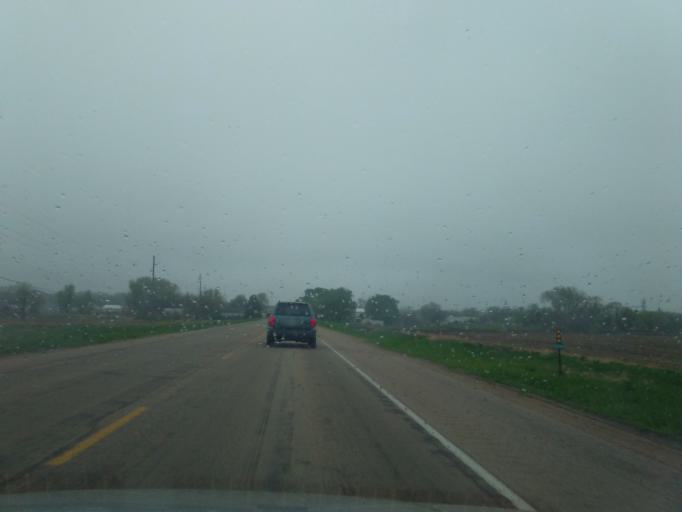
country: US
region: Nebraska
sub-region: Wayne County
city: Wayne
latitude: 42.2220
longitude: -97.0178
